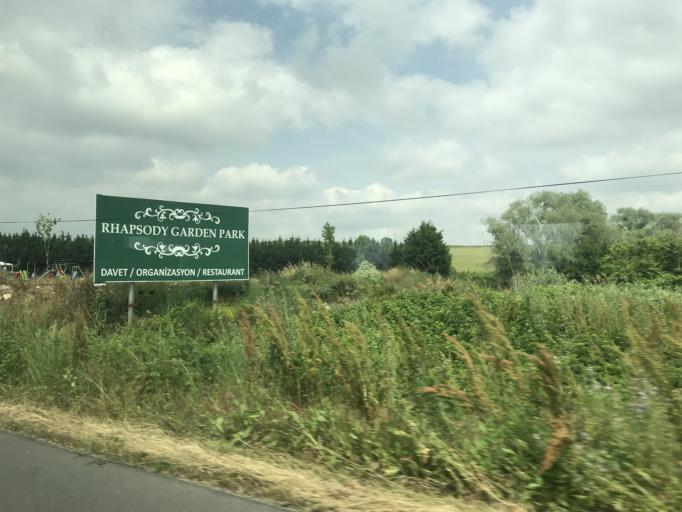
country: TR
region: Tekirdag
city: Tekirdag
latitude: 40.9961
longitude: 27.6374
